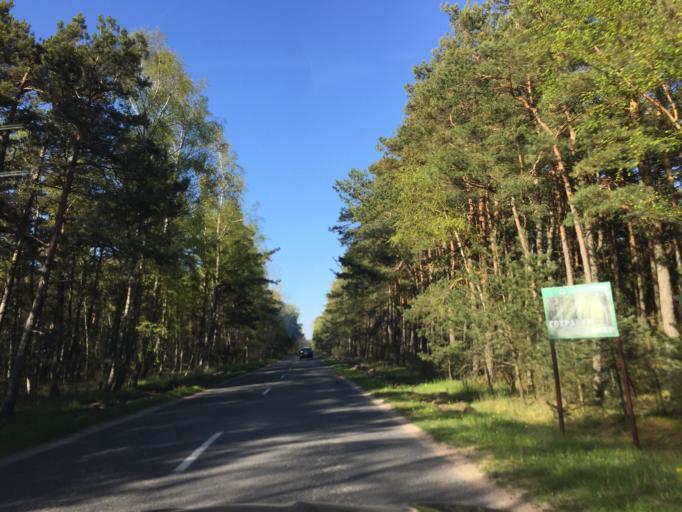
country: LT
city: Nida
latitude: 55.2070
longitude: 20.8757
